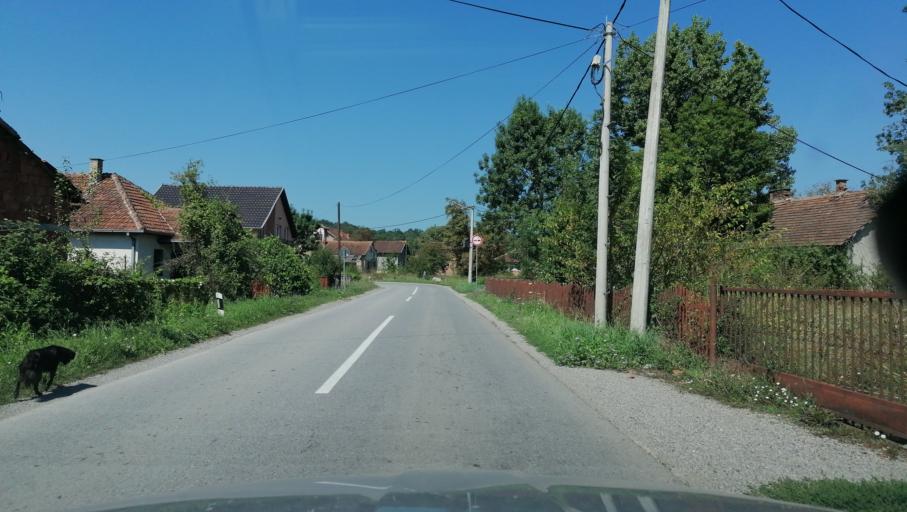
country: RS
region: Central Serbia
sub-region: Raski Okrug
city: Kraljevo
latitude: 43.7251
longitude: 20.8010
